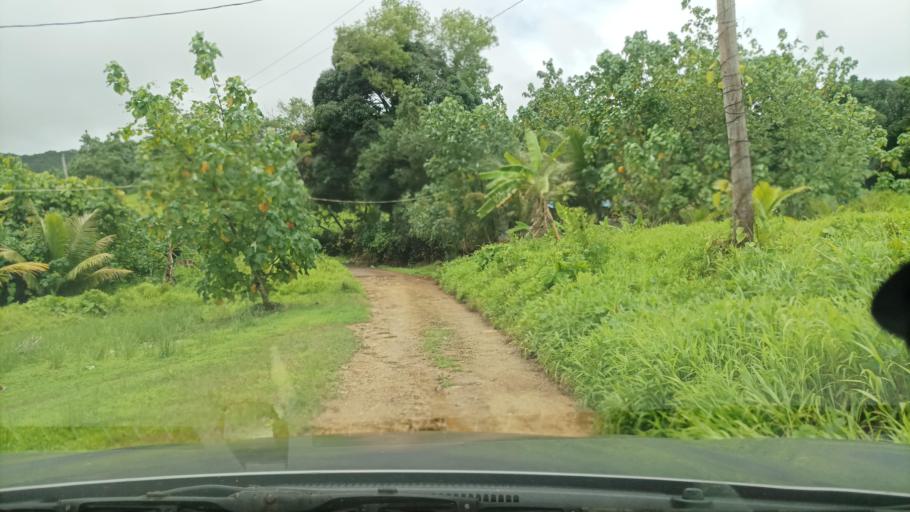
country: FM
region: Pohnpei
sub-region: Madolenihm Municipality
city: Madolenihm Municipality Government
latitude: 6.8897
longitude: 158.2917
